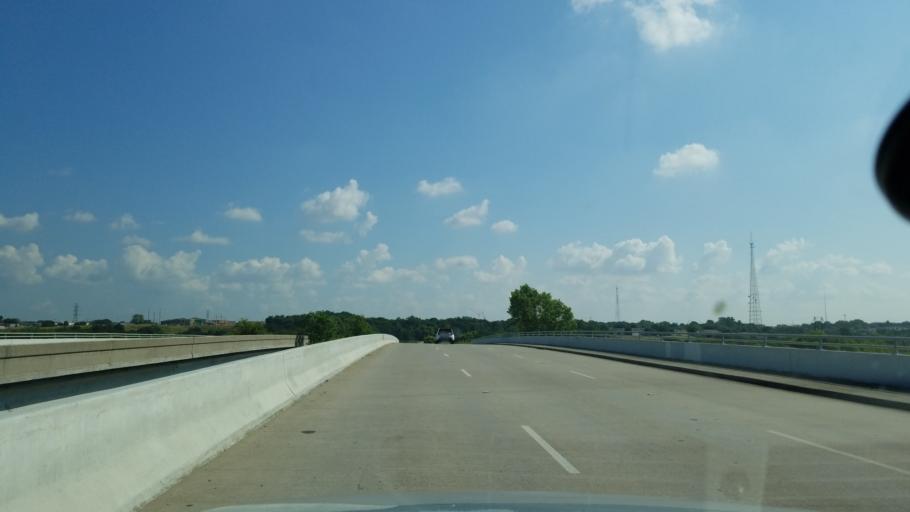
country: US
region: Texas
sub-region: Tarrant County
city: Hurst
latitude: 32.8032
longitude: -97.1417
